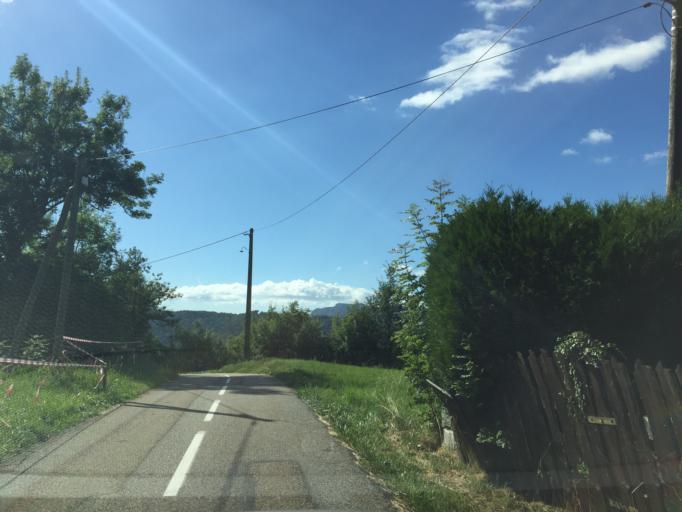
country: FR
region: Rhone-Alpes
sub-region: Departement de la Savoie
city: La Rochette
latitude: 45.4773
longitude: 6.1619
